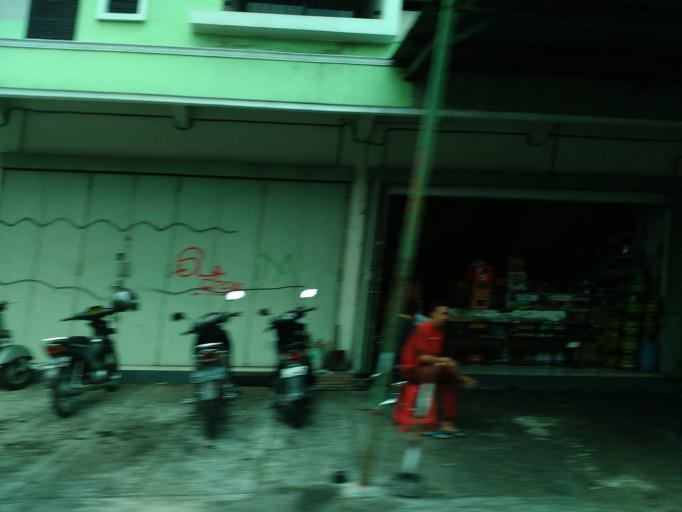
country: ID
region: Central Java
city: Gatak
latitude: -7.6088
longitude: 110.7018
